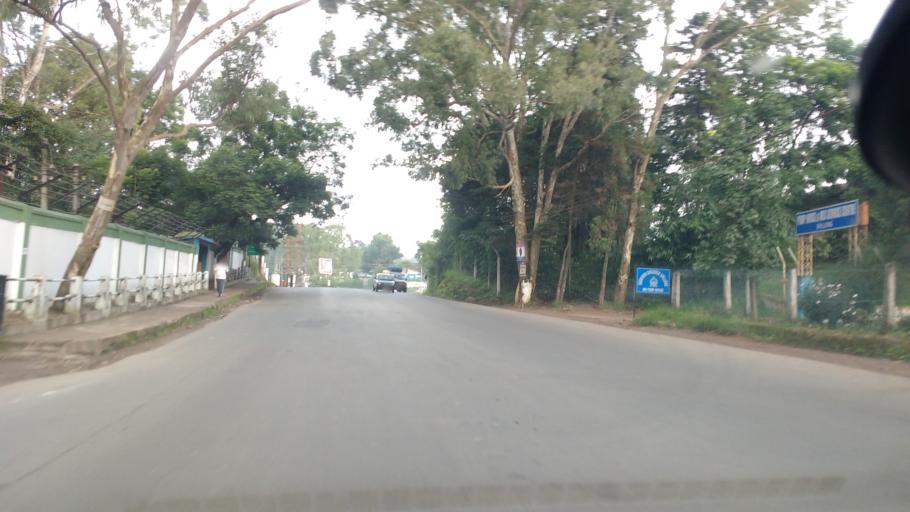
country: IN
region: Meghalaya
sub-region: East Khasi Hills
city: Shillong
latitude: 25.5715
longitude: 91.8724
